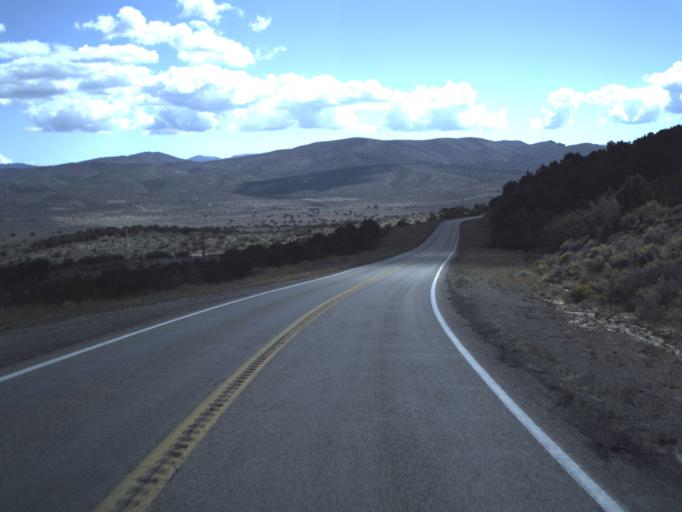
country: US
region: Utah
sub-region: Washington County
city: Enterprise
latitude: 37.5256
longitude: -113.6434
